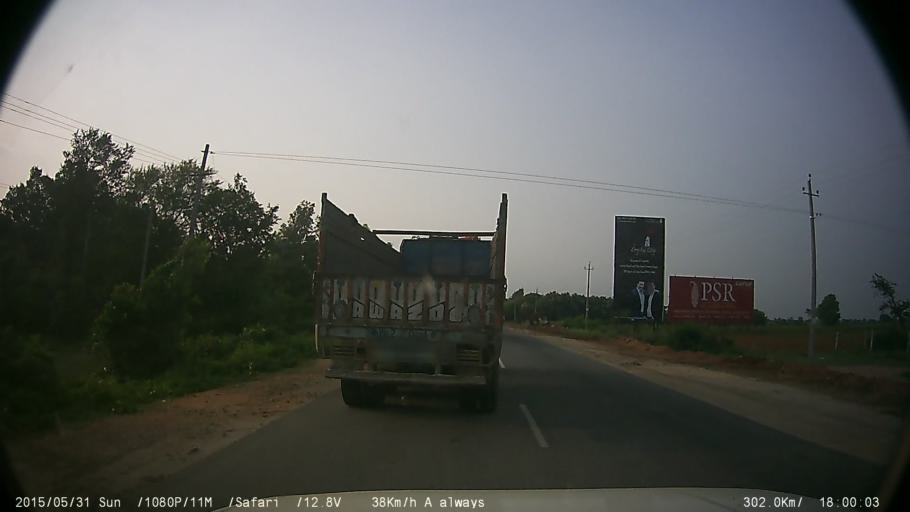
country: IN
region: Karnataka
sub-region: Mysore
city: Nanjangud
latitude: 12.0186
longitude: 76.6727
